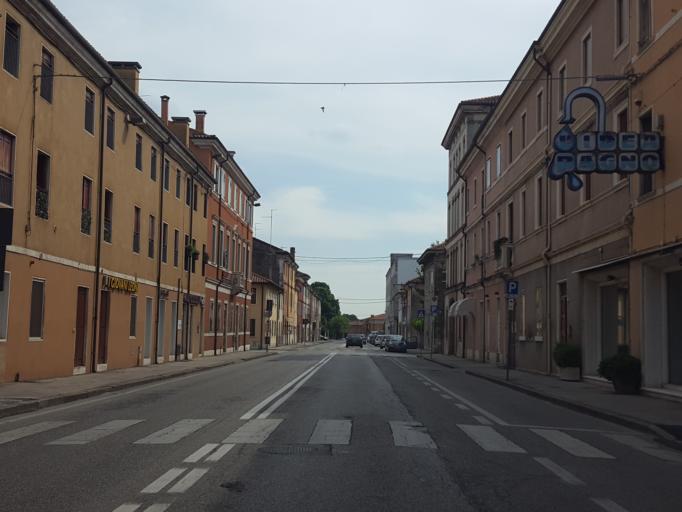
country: IT
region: Veneto
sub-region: Provincia di Vicenza
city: Lonigo
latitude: 45.3866
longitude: 11.3866
